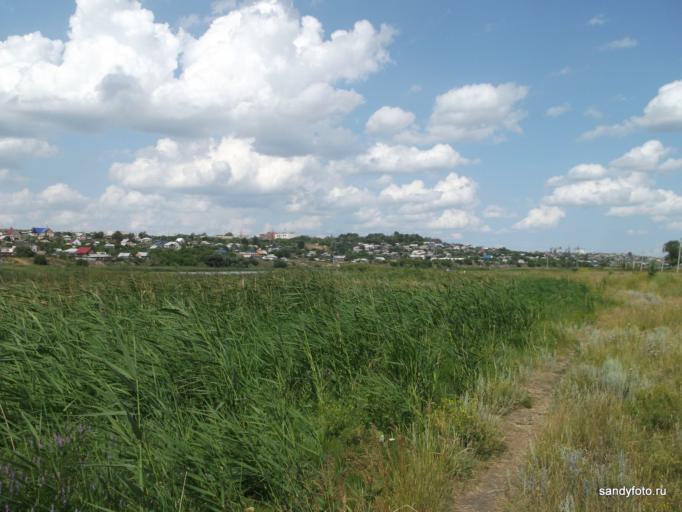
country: RU
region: Chelyabinsk
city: Troitsk
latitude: 54.0934
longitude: 61.5402
